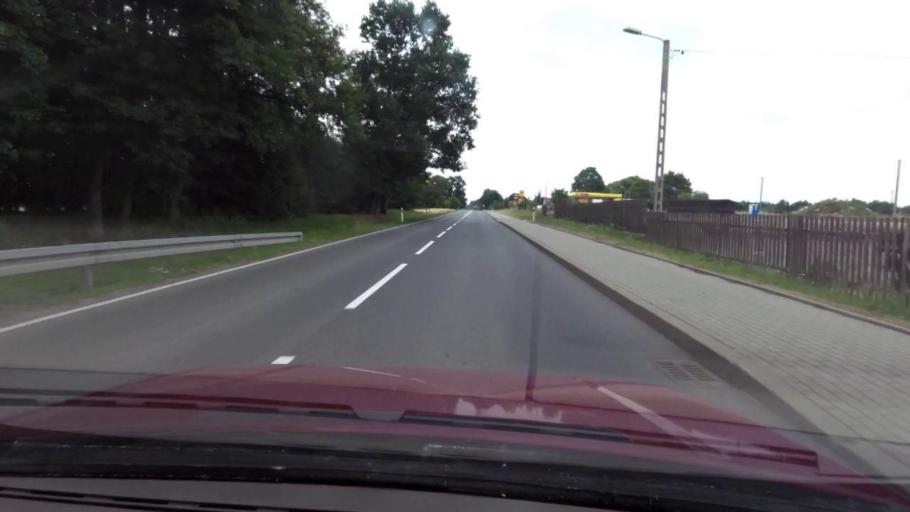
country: PL
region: Pomeranian Voivodeship
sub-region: Powiat bytowski
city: Trzebielino
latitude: 54.2088
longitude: 17.0898
